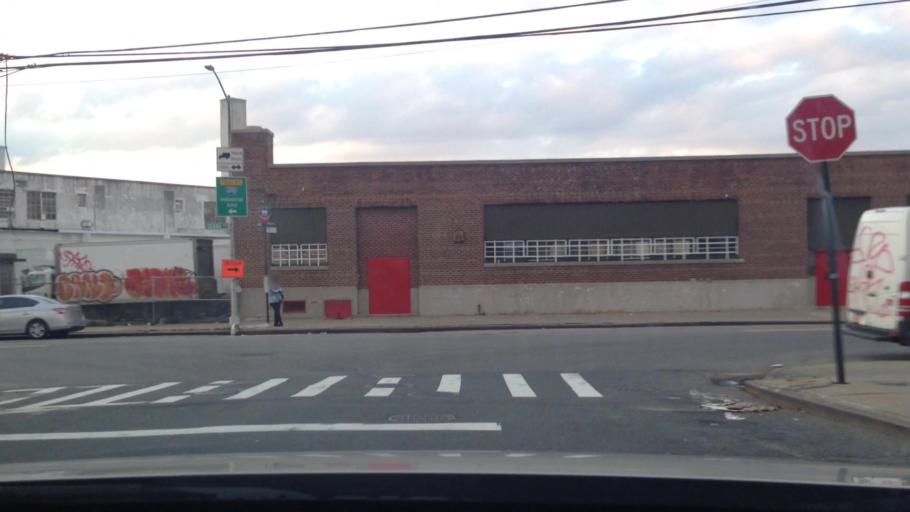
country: US
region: New York
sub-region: Queens County
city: Long Island City
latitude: 40.7184
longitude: -73.9151
